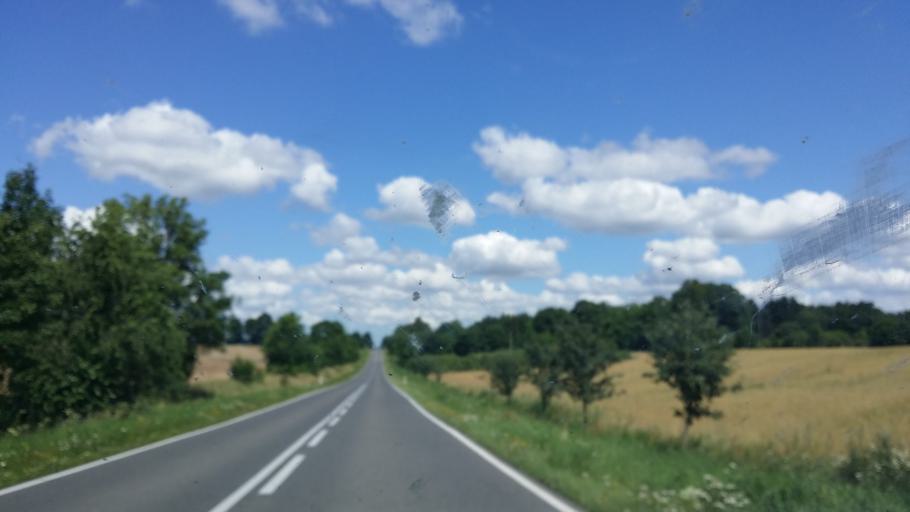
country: PL
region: West Pomeranian Voivodeship
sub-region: Powiat swidwinski
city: Slawoborze
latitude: 53.8511
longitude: 15.7344
